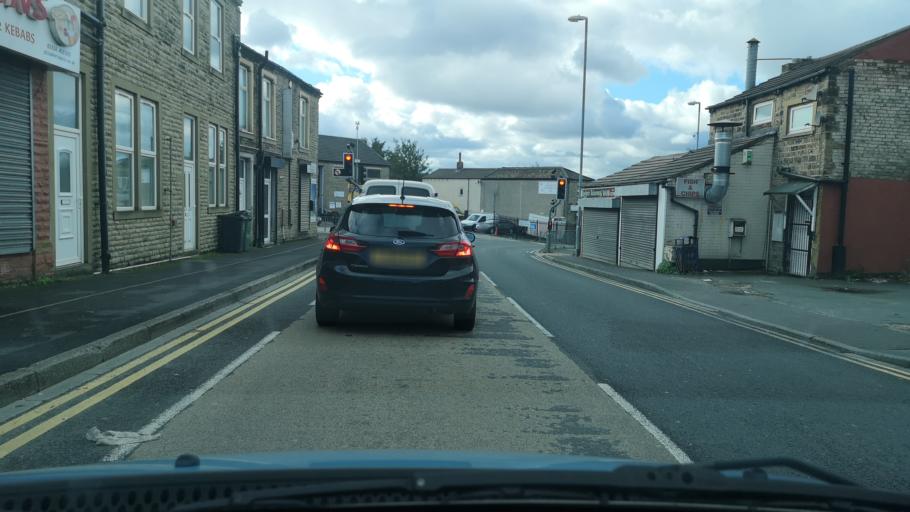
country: GB
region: England
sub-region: Kirklees
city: Heckmondwike
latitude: 53.7096
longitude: -1.6609
